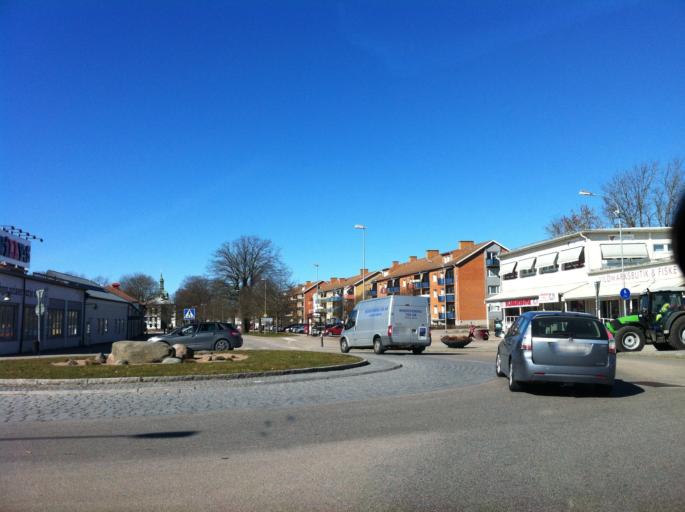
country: SE
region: Vaestra Goetaland
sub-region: Vanersborgs Kommun
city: Vargon
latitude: 58.3563
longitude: 12.4131
